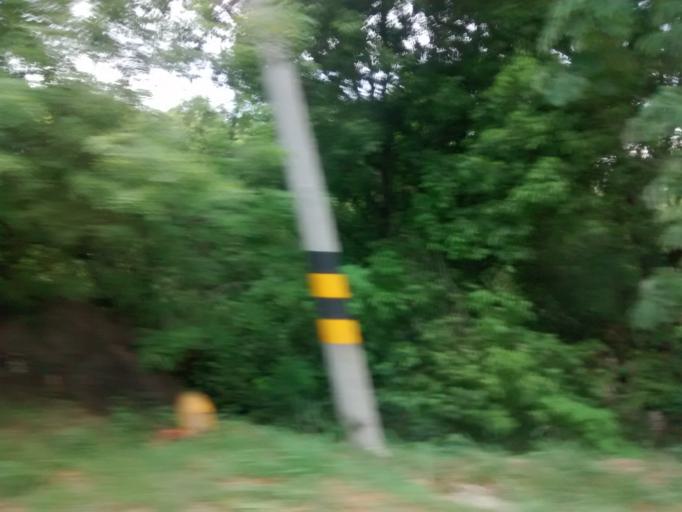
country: CO
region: Cundinamarca
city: Ricaurte
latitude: 4.2488
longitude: -74.7328
